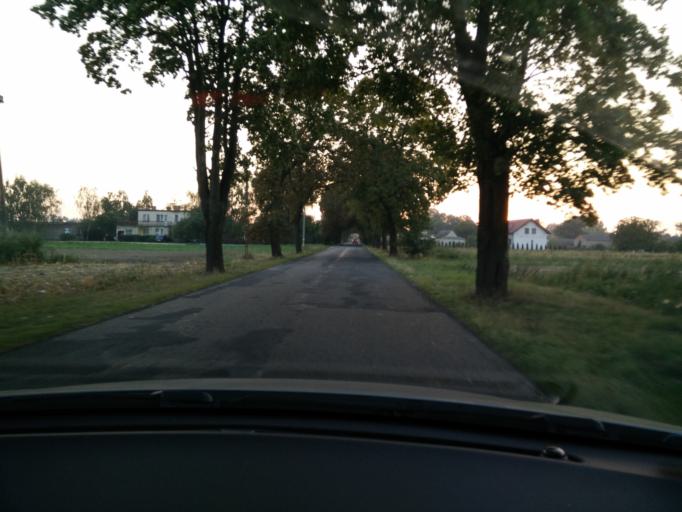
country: PL
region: Greater Poland Voivodeship
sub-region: Powiat sredzki
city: Dominowo
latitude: 52.2133
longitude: 17.3884
